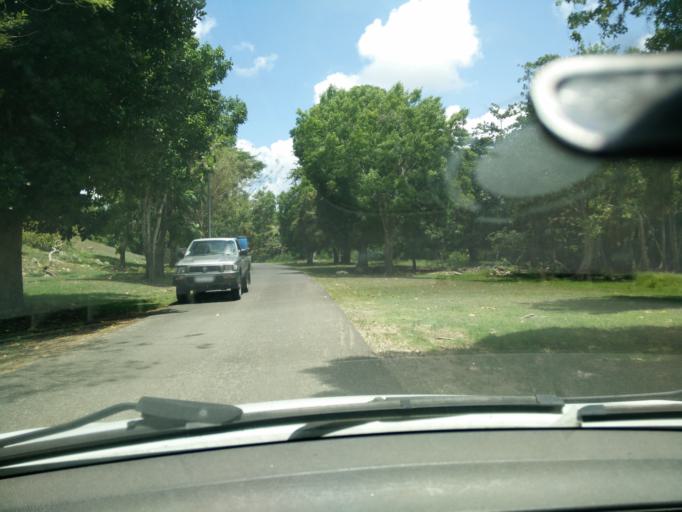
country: GP
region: Guadeloupe
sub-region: Guadeloupe
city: Petit-Canal
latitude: 16.3784
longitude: -61.4927
